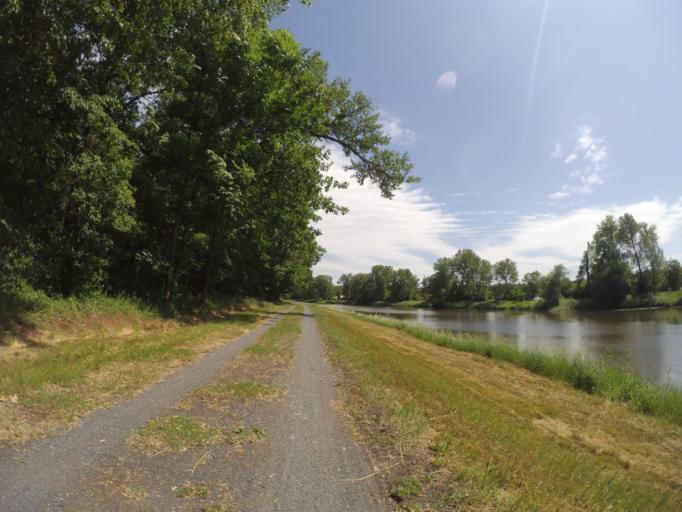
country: CZ
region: Central Bohemia
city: Poricany
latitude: 50.1671
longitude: 14.9090
